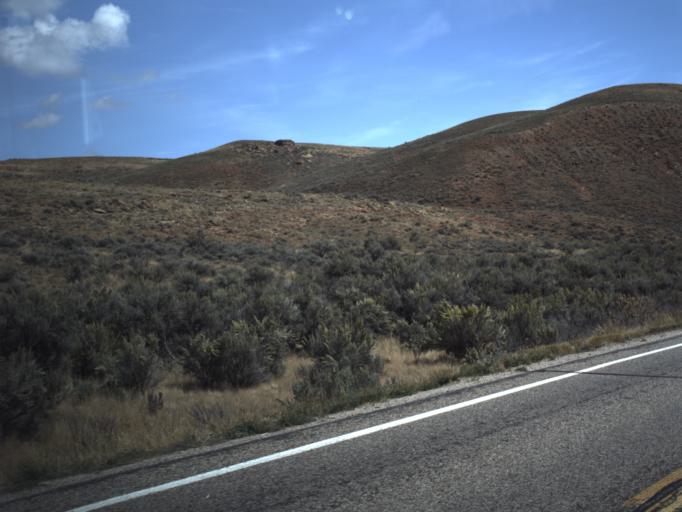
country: US
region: Utah
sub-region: Rich County
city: Randolph
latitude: 41.7759
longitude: -111.1813
